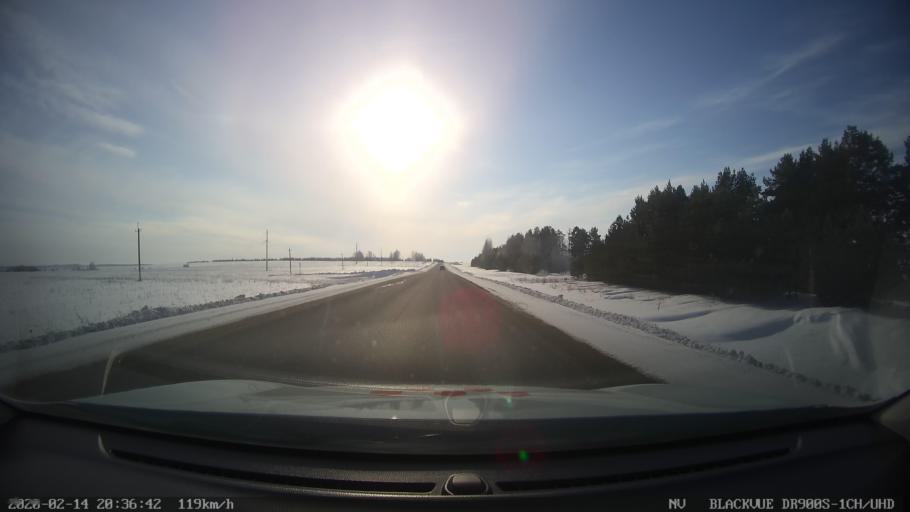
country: RU
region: Tatarstan
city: Kuybyshevskiy Zaton
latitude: 55.3629
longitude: 49.0019
